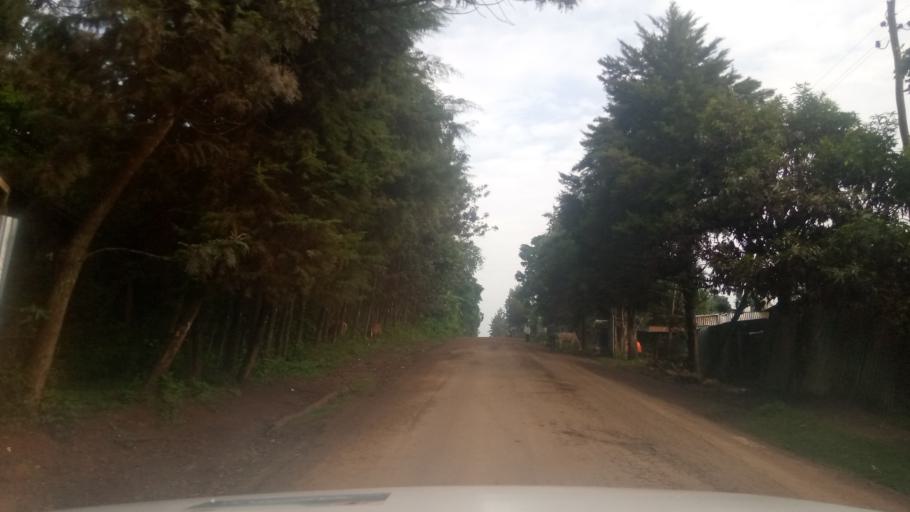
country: ET
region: Oromiya
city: Agaro
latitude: 7.8399
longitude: 36.6637
